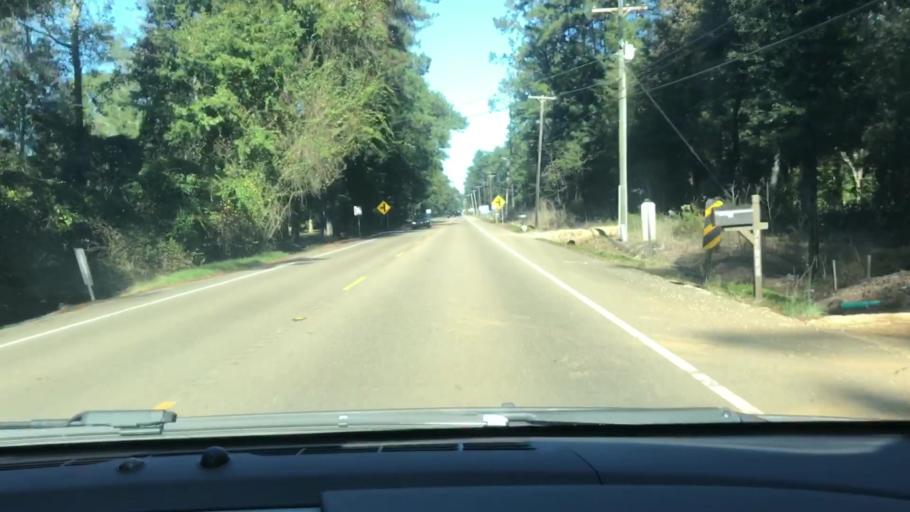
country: US
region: Louisiana
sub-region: Saint Tammany Parish
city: Abita Springs
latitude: 30.5206
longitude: -90.0472
